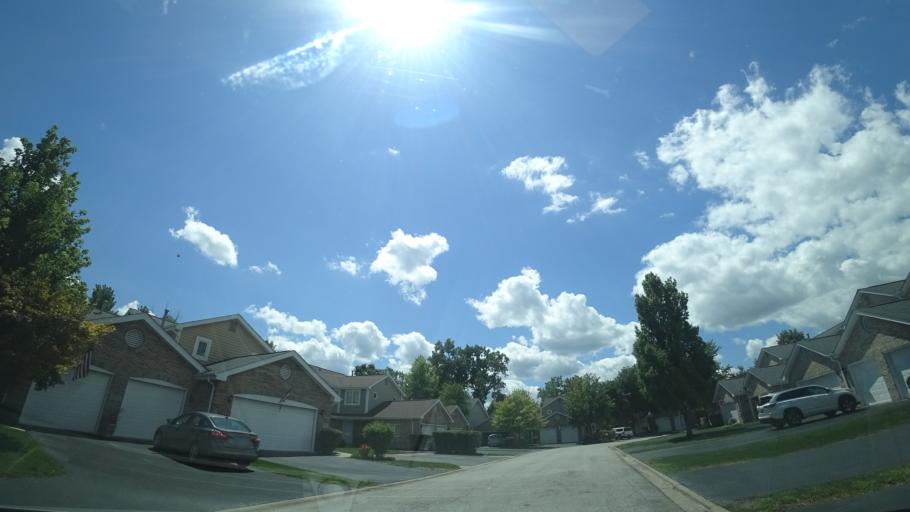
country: US
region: Illinois
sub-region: Will County
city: Mokena
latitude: 41.5738
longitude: -87.8928
